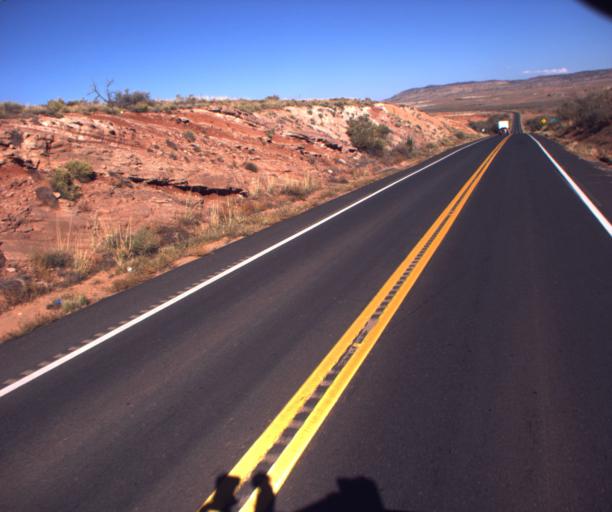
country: US
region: Arizona
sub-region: Coconino County
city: Kaibito
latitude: 36.3205
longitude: -110.9436
